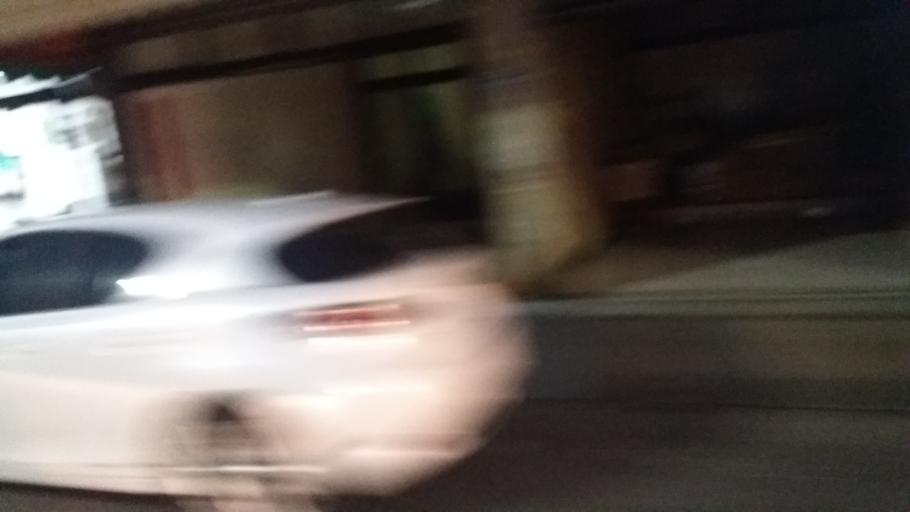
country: TW
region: Taiwan
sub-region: Hsinchu
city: Hsinchu
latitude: 24.7626
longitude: 120.9132
